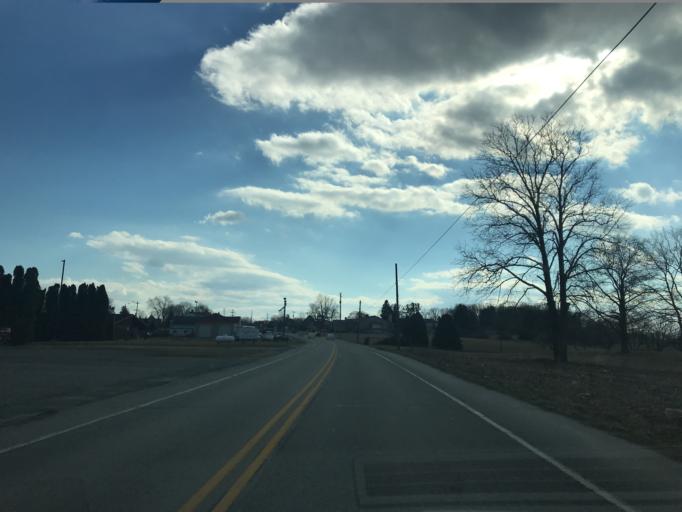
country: US
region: Pennsylvania
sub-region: Chester County
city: Oxford
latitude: 39.7524
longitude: -76.0163
